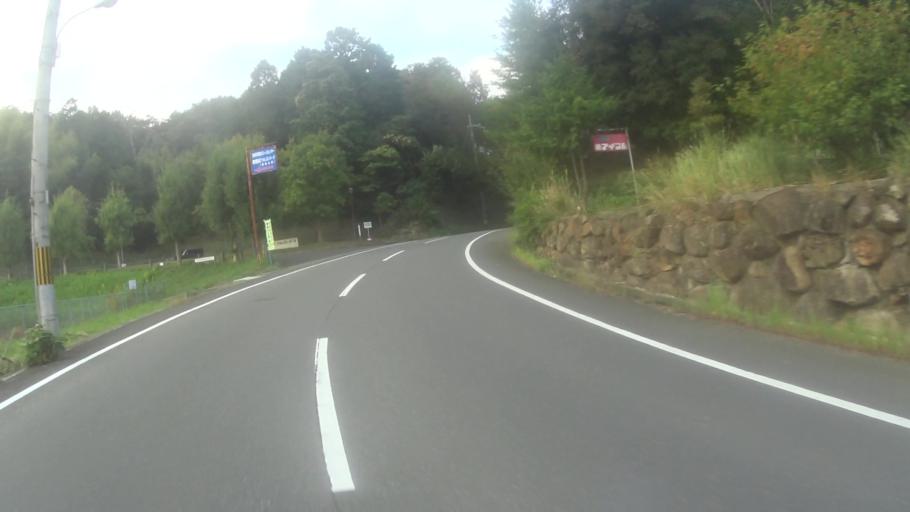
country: JP
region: Kyoto
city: Miyazu
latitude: 35.5253
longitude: 135.0919
